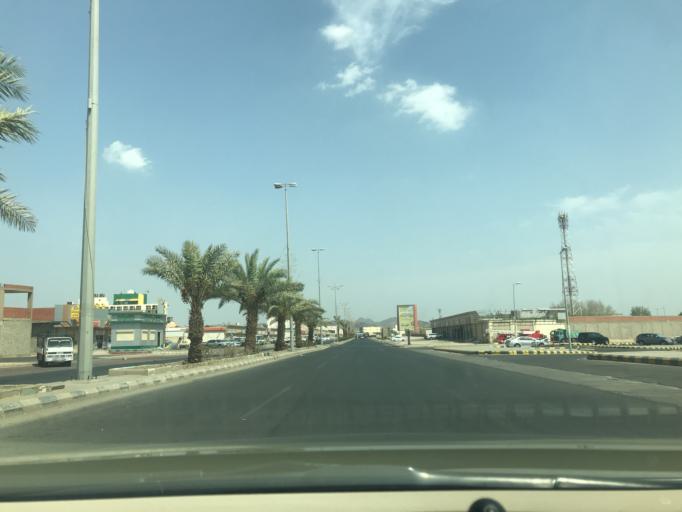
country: SA
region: Makkah
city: Al Jumum
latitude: 21.6200
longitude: 39.6863
